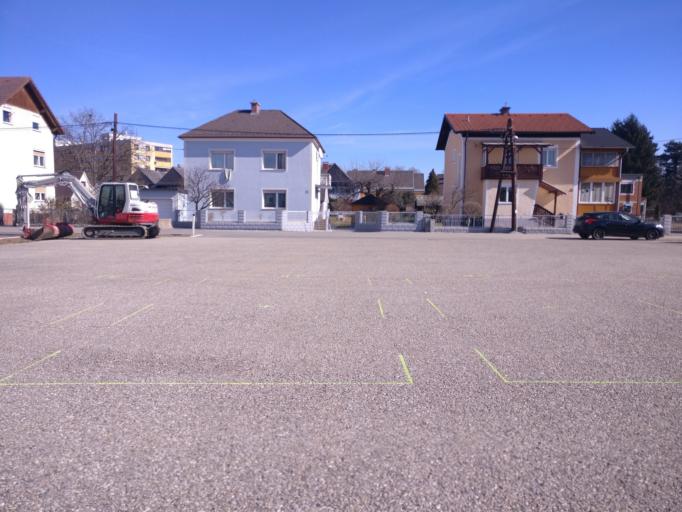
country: AT
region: Styria
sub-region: Politischer Bezirk Graz-Umgebung
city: Feldkirchen bei Graz
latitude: 47.0128
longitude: 15.4485
